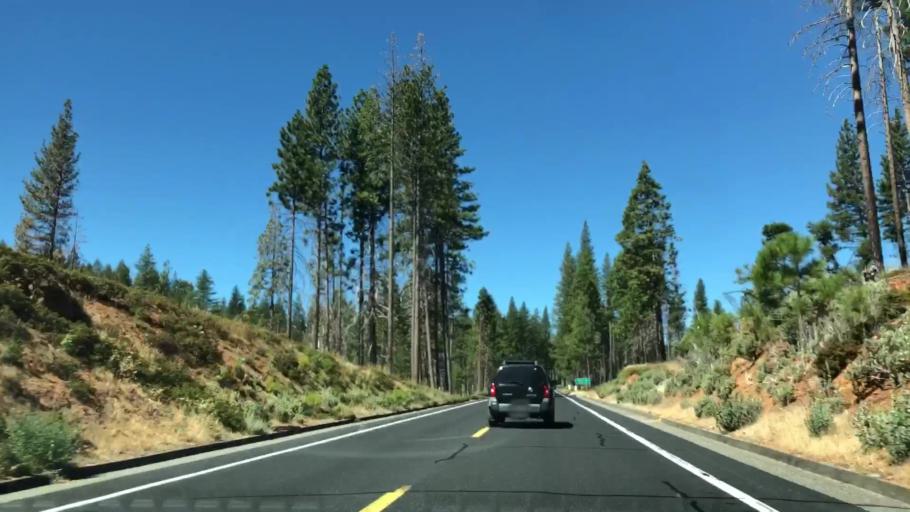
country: US
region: California
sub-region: Mariposa County
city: Midpines
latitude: 37.8221
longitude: -119.9624
